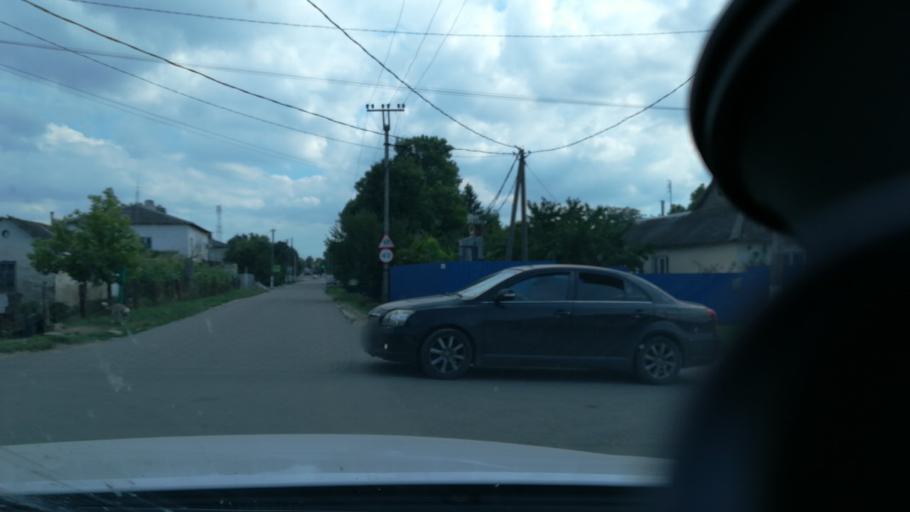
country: RU
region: Krasnodarskiy
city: Yurovka
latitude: 45.1173
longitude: 37.4152
